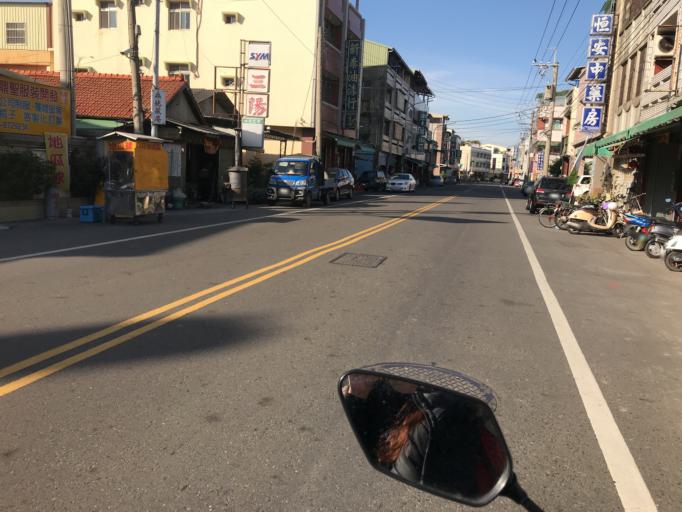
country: TW
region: Taiwan
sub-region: Nantou
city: Nantou
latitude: 23.8907
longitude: 120.5875
